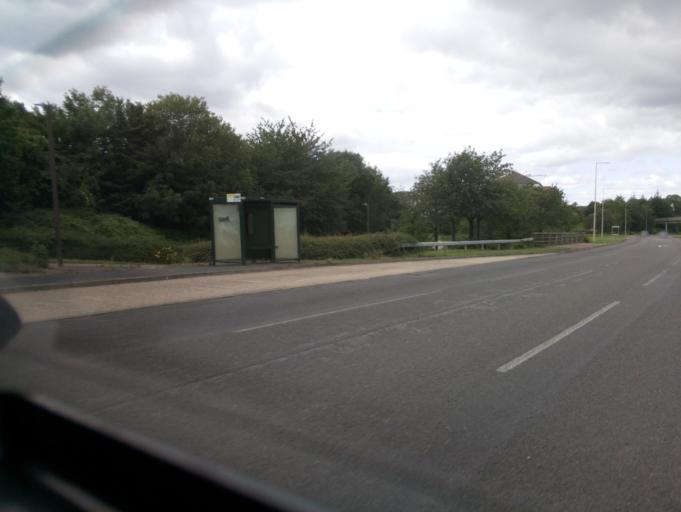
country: GB
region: England
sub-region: Milton Keynes
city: Shenley Church End
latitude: 52.0183
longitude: -0.7891
